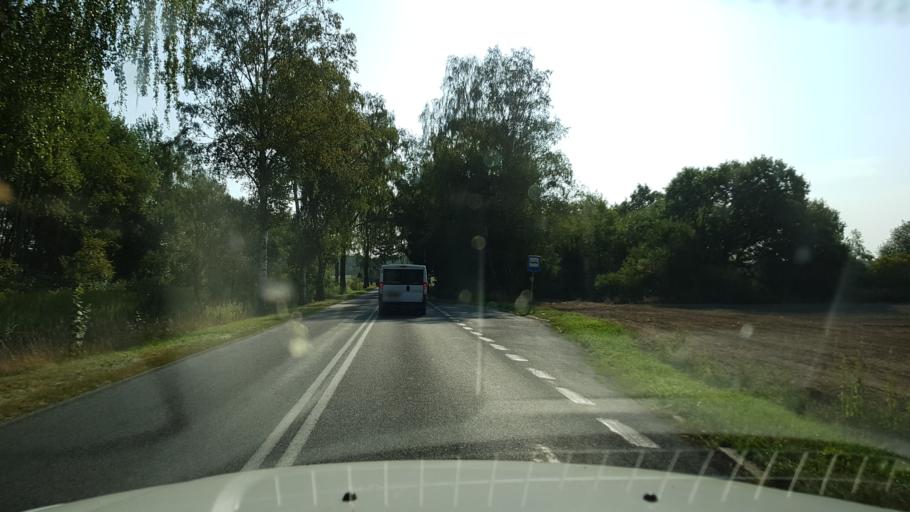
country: PL
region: West Pomeranian Voivodeship
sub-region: Powiat gryficki
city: Ploty
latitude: 53.7877
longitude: 15.3198
